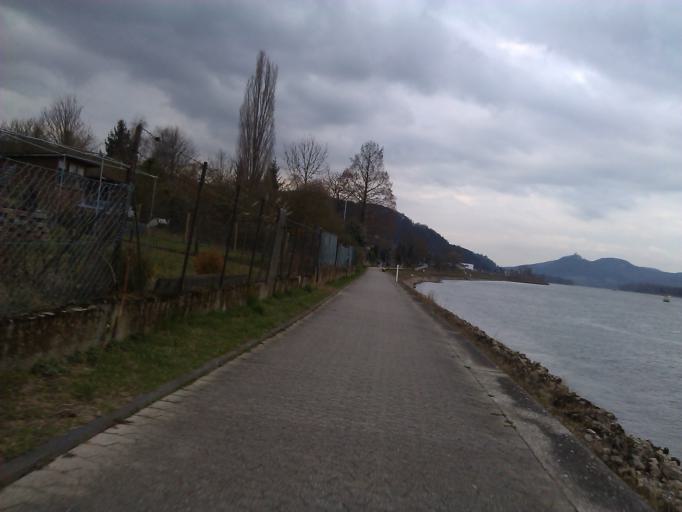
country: DE
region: Rheinland-Pfalz
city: Unkel
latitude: 50.6088
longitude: 7.2114
